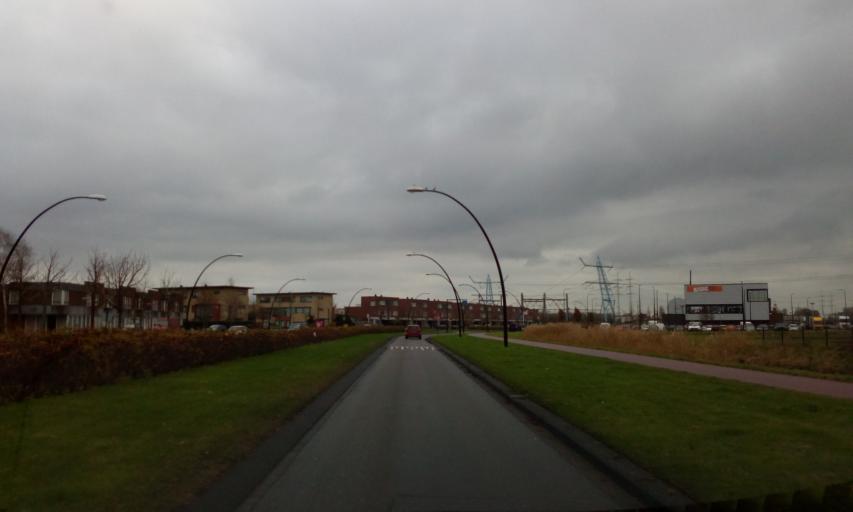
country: NL
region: South Holland
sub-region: Gemeente Rijswijk
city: Rijswijk
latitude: 52.0192
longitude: 4.3002
